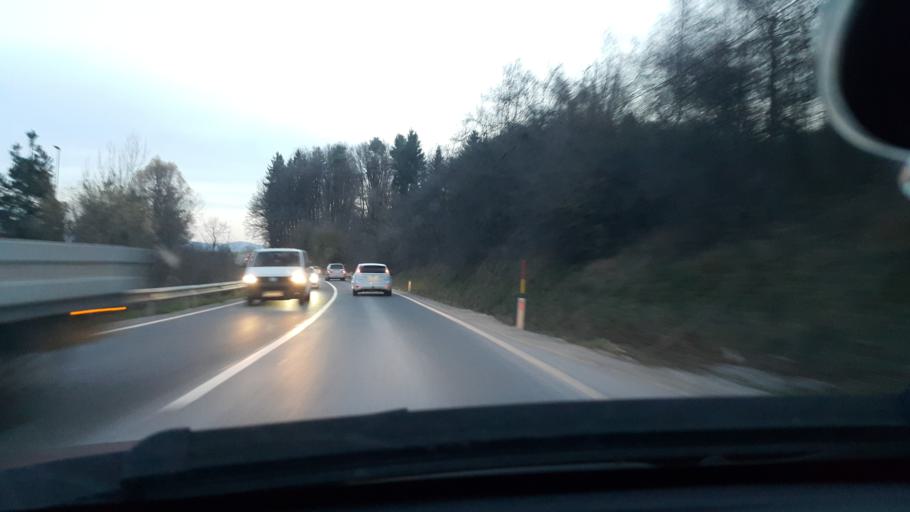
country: SI
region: Zalec
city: Gotovlje
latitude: 46.2906
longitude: 15.1739
